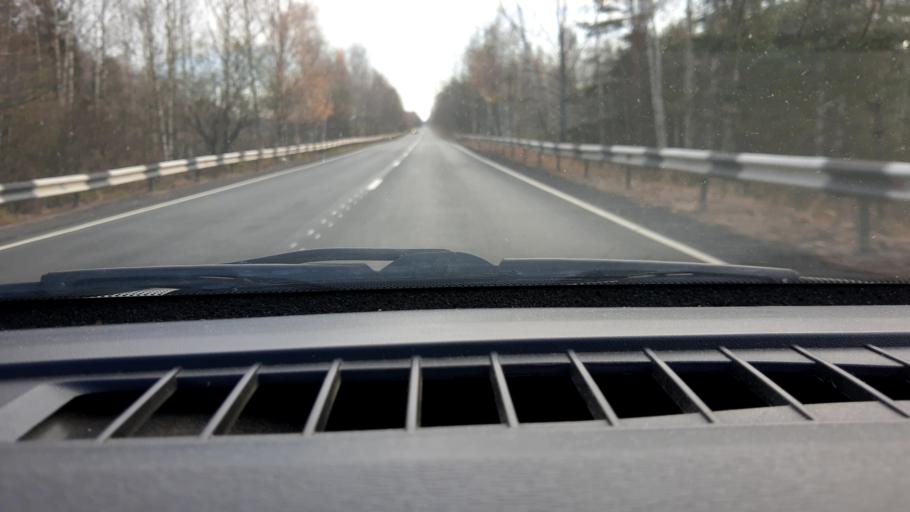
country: RU
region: Nizjnij Novgorod
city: Novaya Balakhna
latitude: 56.5685
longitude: 43.7145
